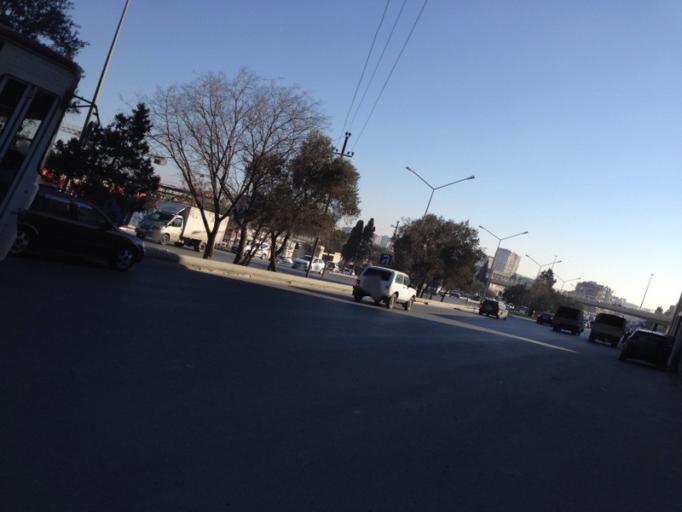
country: AZ
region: Baki
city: Baku
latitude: 40.4175
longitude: 49.8573
